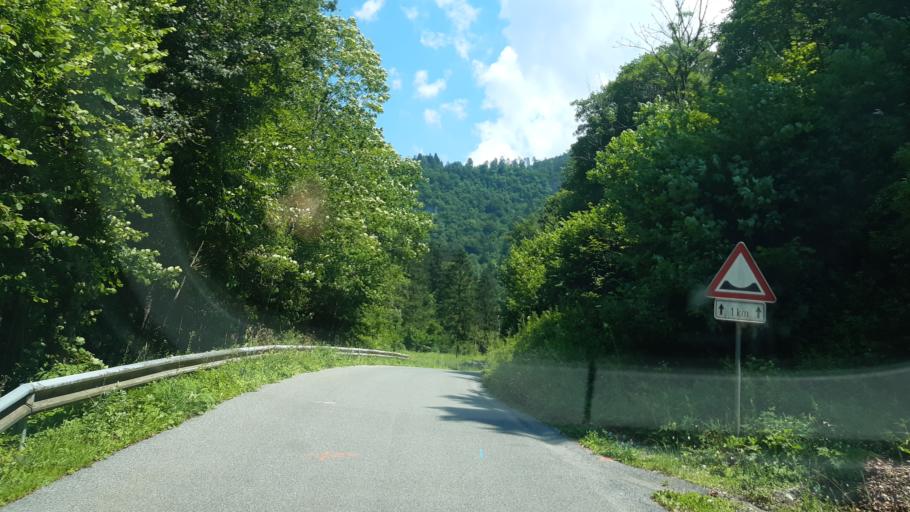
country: SI
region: Cerklje na Gorenjskem
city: Cerklje na Gorenjskem
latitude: 46.2746
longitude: 14.4945
